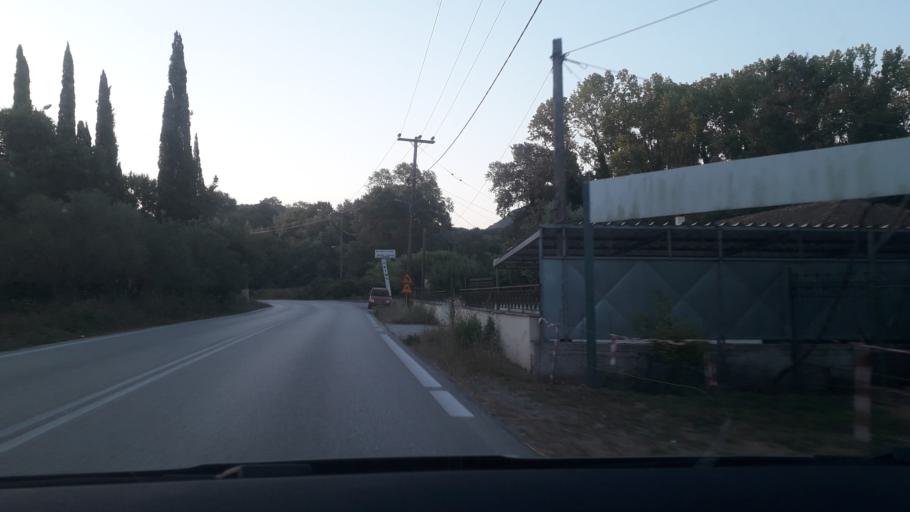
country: GR
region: Ionian Islands
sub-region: Nomos Kerkyras
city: Agios Matthaios
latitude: 39.4771
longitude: 19.9189
